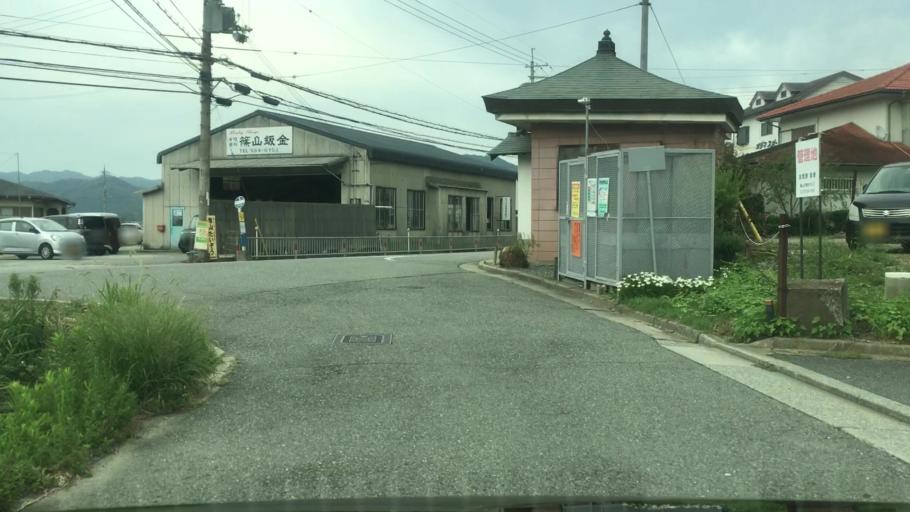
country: JP
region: Hyogo
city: Sasayama
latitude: 35.0654
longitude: 135.1933
